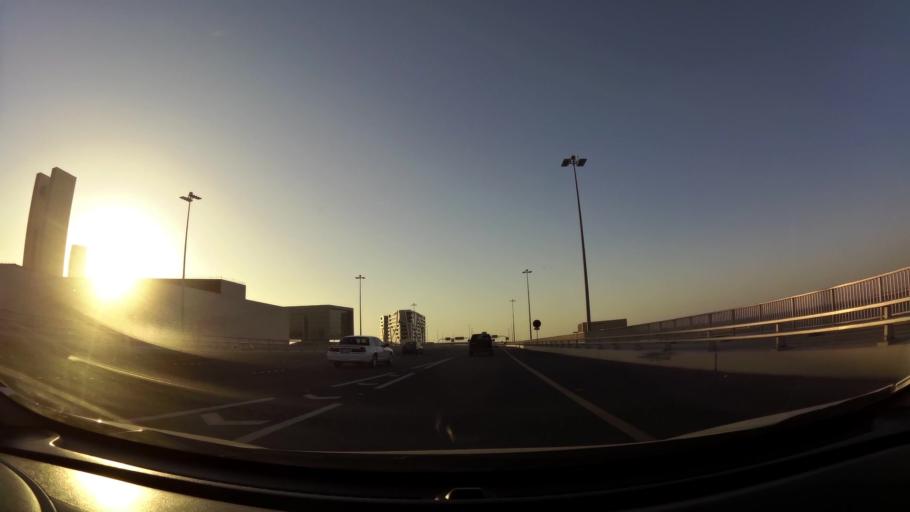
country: BH
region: Muharraq
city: Al Muharraq
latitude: 26.2489
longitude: 50.5876
